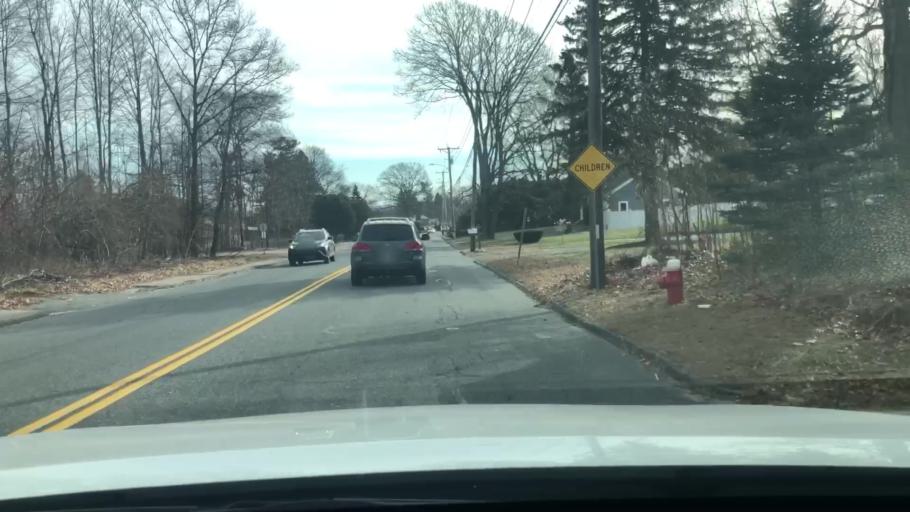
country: US
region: Massachusetts
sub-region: Worcester County
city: Hopedale
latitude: 42.1463
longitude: -71.5381
